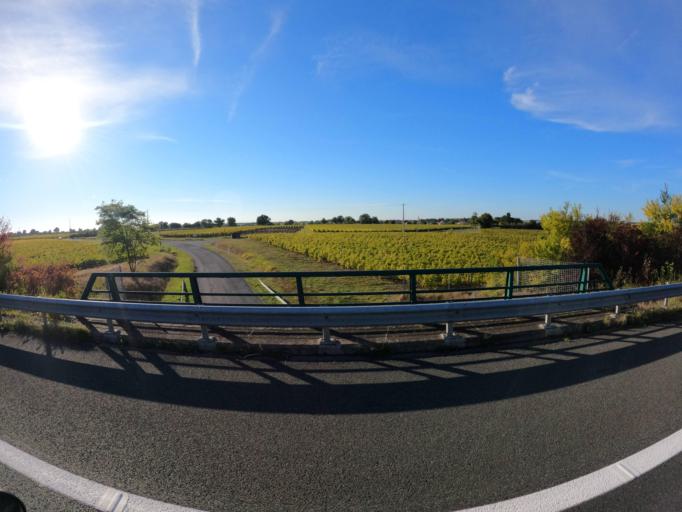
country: FR
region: Pays de la Loire
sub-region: Departement de Maine-et-Loire
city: Saint-Lambert-du-Lattay
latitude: 47.2917
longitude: -0.6130
